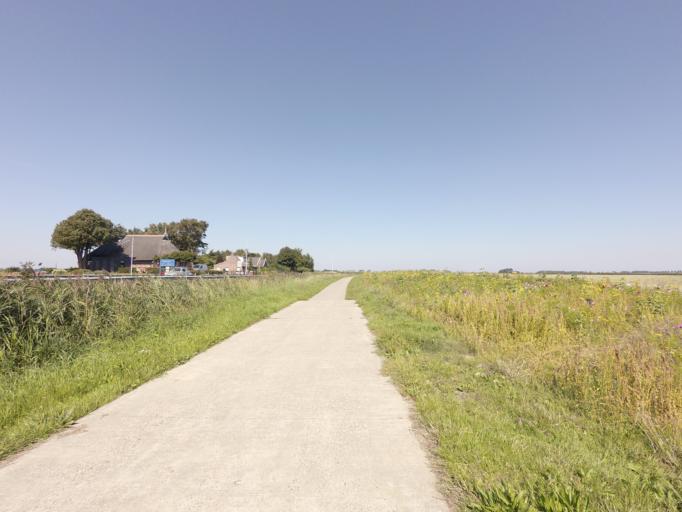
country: NL
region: Friesland
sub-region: Gemeente Dongeradeel
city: Anjum
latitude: 53.3826
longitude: 6.0563
